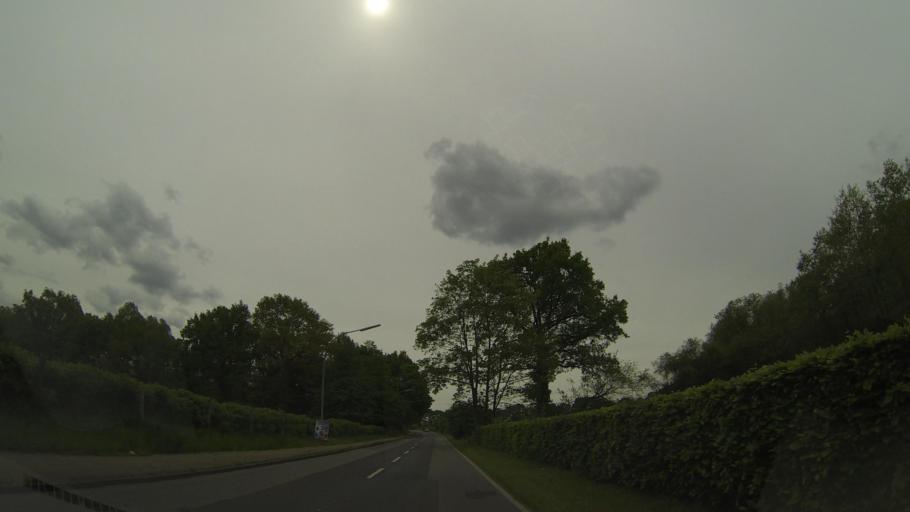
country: DE
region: Schleswig-Holstein
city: Ellerbek
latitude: 53.6400
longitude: 9.8711
